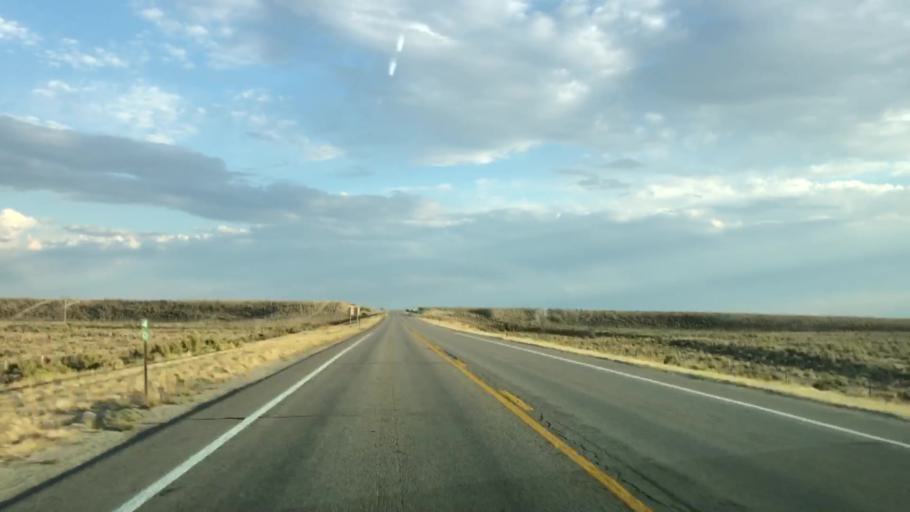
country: US
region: Wyoming
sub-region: Sweetwater County
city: North Rock Springs
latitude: 42.1027
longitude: -109.4469
